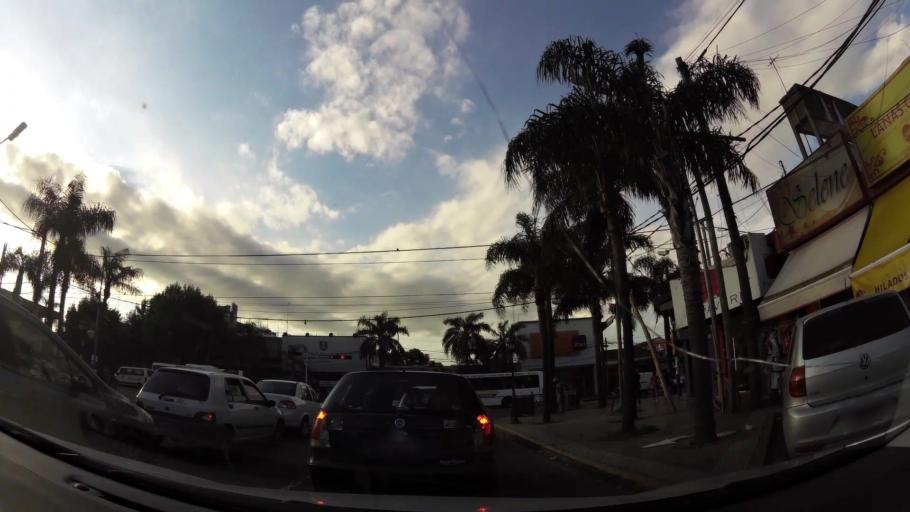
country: AR
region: Buenos Aires
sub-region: Partido de Tigre
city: Tigre
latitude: -34.4589
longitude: -58.6310
